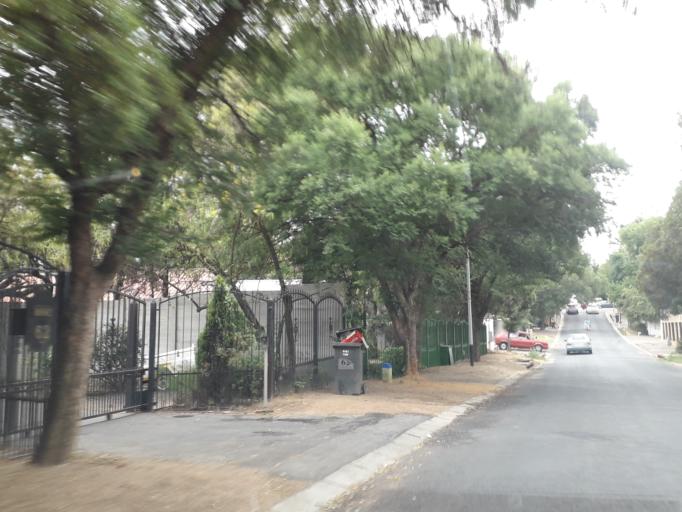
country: ZA
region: Gauteng
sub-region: City of Johannesburg Metropolitan Municipality
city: Roodepoort
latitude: -26.1024
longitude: 27.9684
